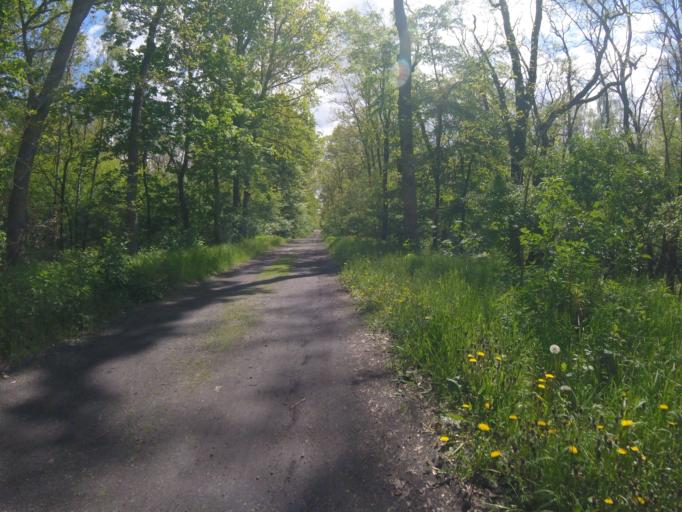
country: DE
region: Brandenburg
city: Konigs Wusterhausen
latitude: 52.3040
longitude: 13.6125
